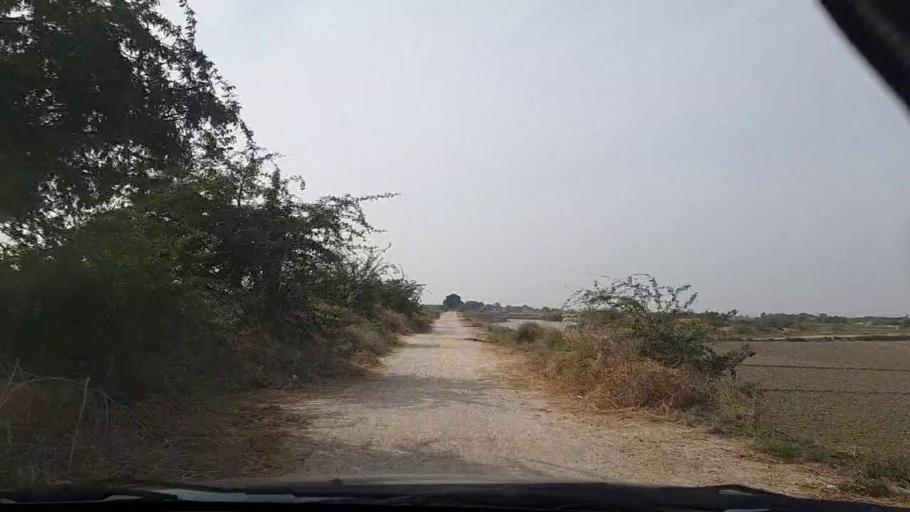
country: PK
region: Sindh
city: Thatta
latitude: 24.5703
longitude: 67.8732
